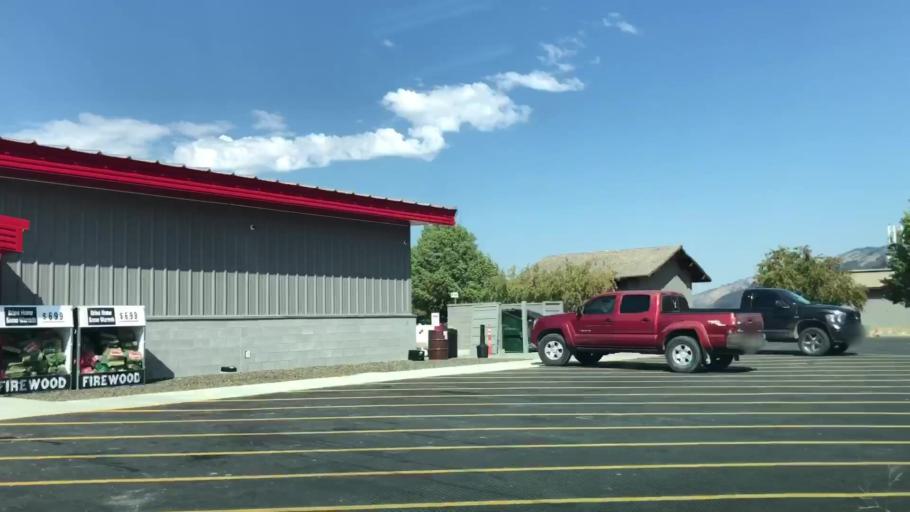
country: US
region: Wyoming
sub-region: Teton County
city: Hoback
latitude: 43.1731
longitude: -111.0171
